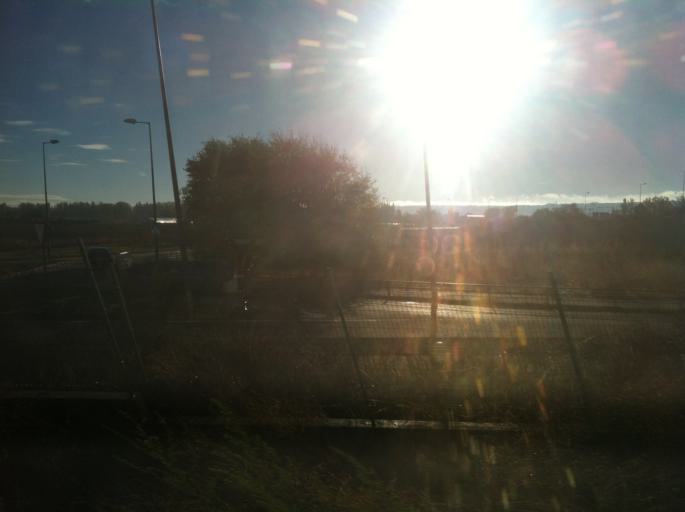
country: ES
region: Castille and Leon
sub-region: Provincia de Valladolid
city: Valladolid
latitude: 41.6653
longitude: -4.7006
